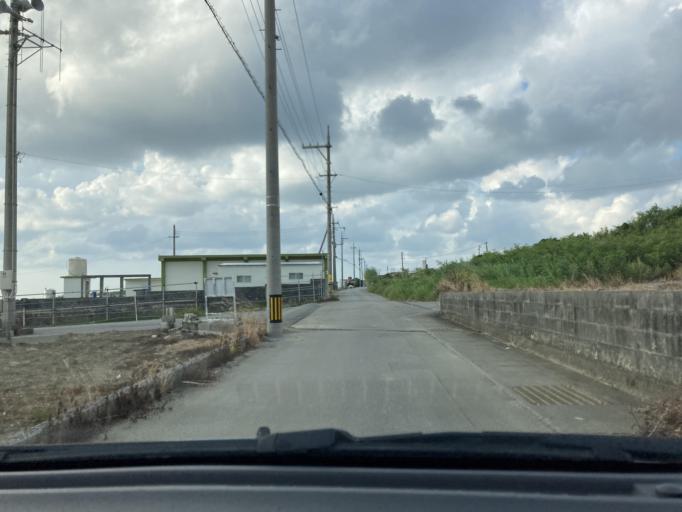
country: JP
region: Okinawa
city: Itoman
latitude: 26.0856
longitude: 127.6627
